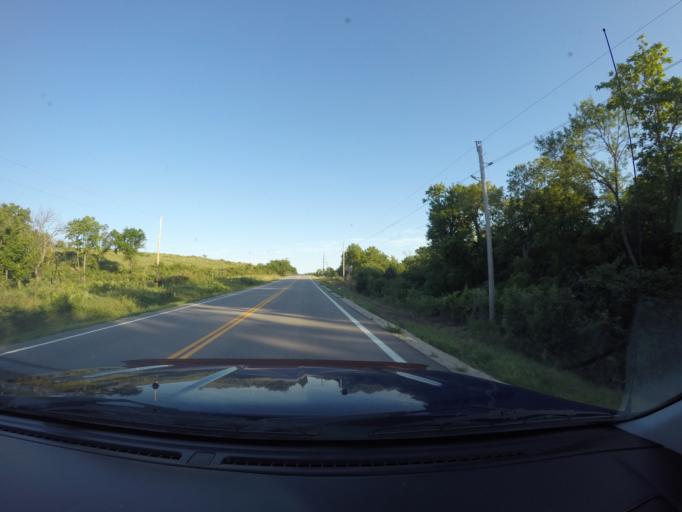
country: US
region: Kansas
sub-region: Pottawatomie County
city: Wamego
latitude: 39.1229
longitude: -96.2933
